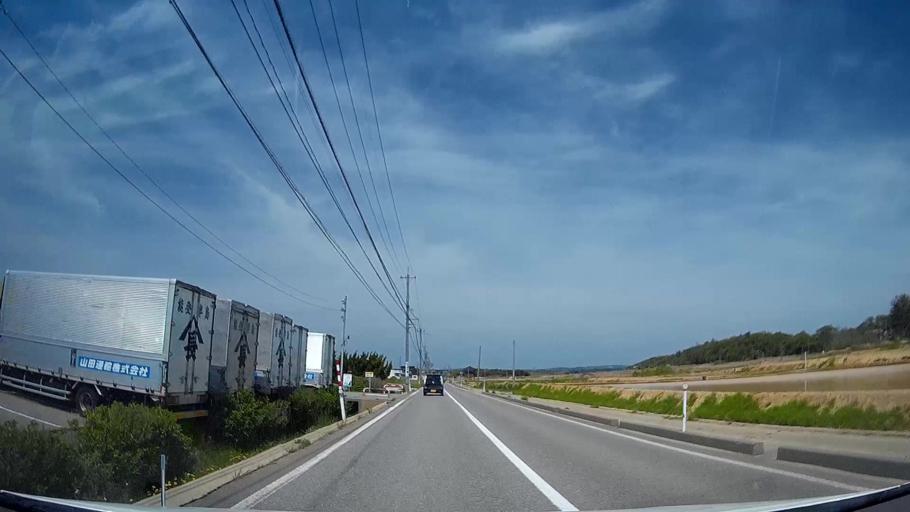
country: JP
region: Ishikawa
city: Hakui
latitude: 36.9370
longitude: 136.7589
